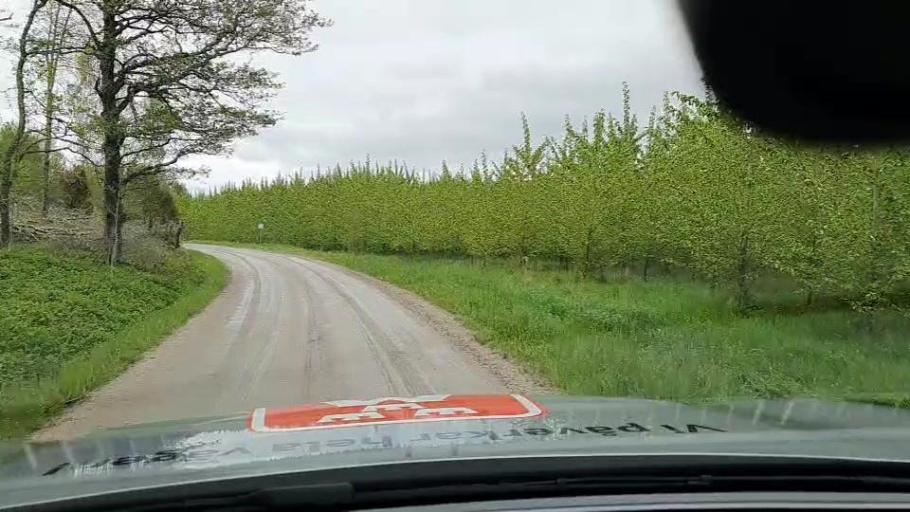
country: SE
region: Soedermanland
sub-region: Nykopings Kommun
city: Svalsta
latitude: 58.6303
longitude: 16.9386
